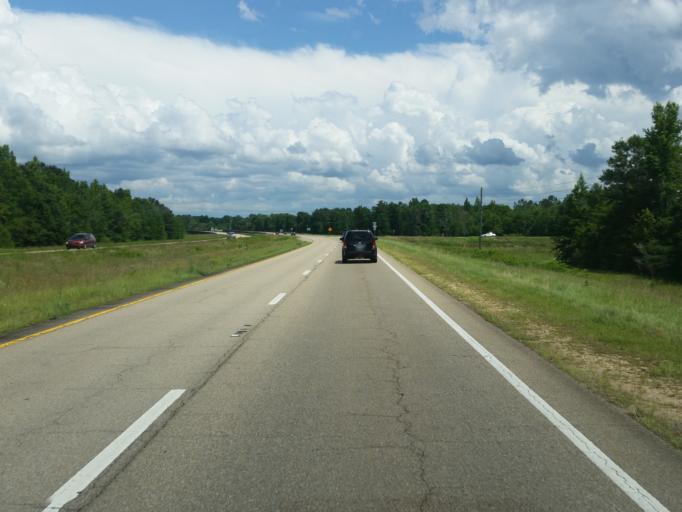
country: US
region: Mississippi
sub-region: Perry County
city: New Augusta
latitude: 31.1106
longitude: -88.8162
